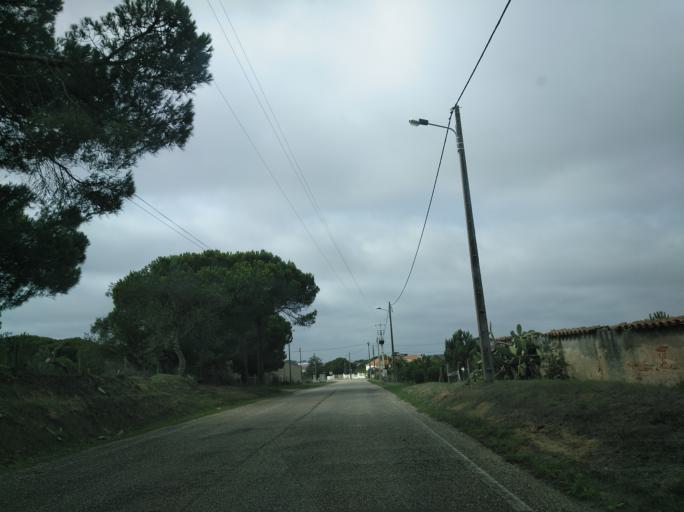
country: PT
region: Setubal
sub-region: Santiago do Cacem
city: Santo Andre
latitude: 38.1368
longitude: -8.7578
